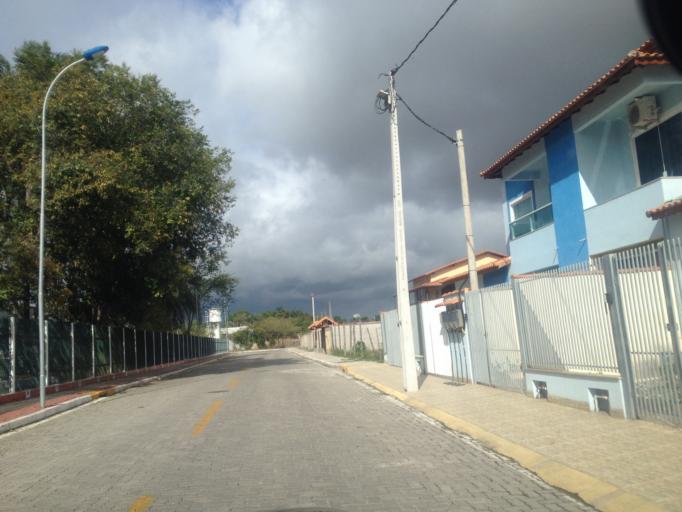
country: BR
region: Rio de Janeiro
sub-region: Porto Real
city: Porto Real
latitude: -22.4126
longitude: -44.2980
